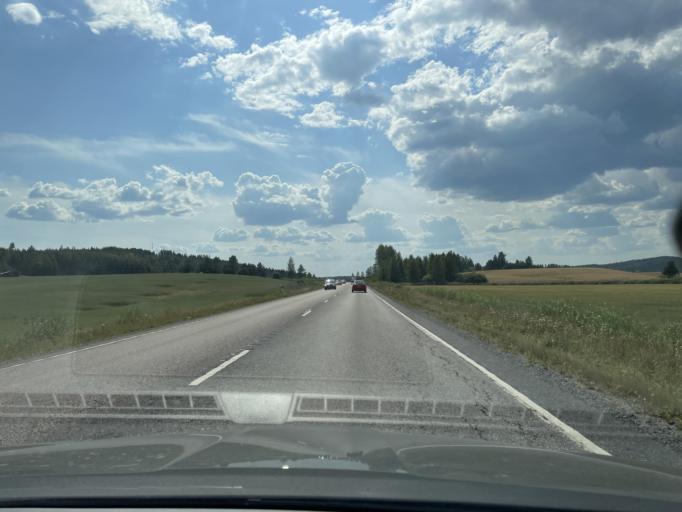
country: FI
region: Central Finland
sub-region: Jyvaeskylae
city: Korpilahti
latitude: 61.9695
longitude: 25.3856
